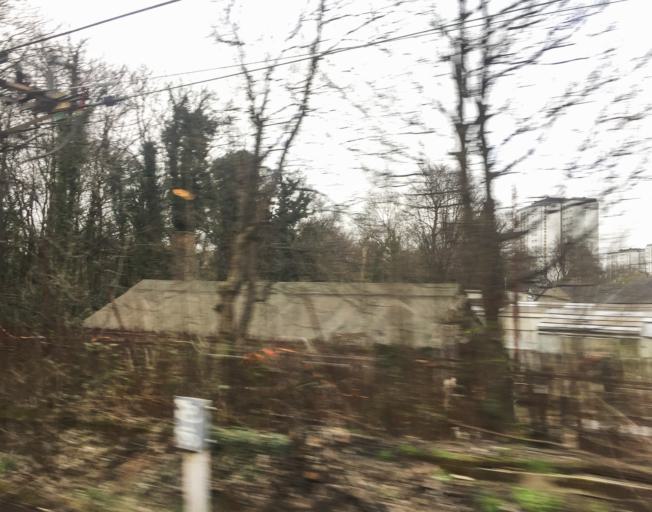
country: GB
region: Scotland
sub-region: West Dunbartonshire
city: Duntocher
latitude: 55.9140
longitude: -4.4322
